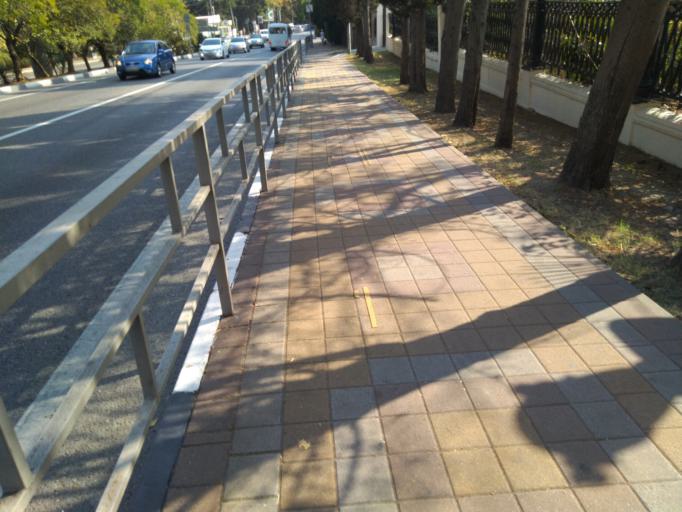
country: RU
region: Krasnodarskiy
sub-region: Sochi City
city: Sochi
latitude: 43.5947
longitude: 39.7175
